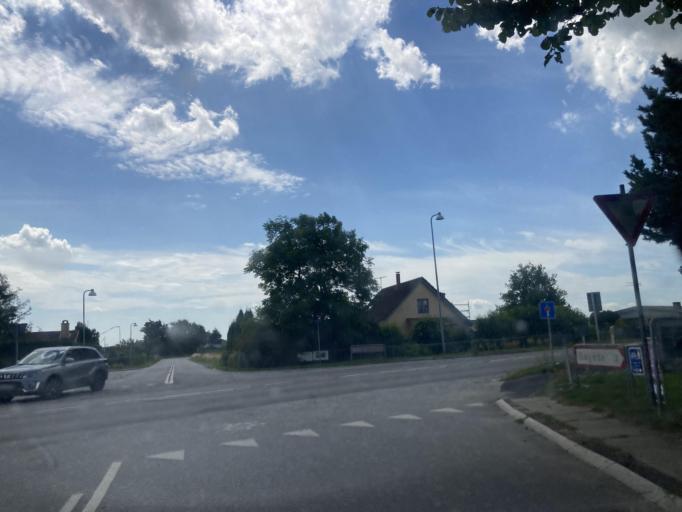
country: DK
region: Zealand
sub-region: Koge Kommune
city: Borup
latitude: 55.4472
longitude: 11.9519
